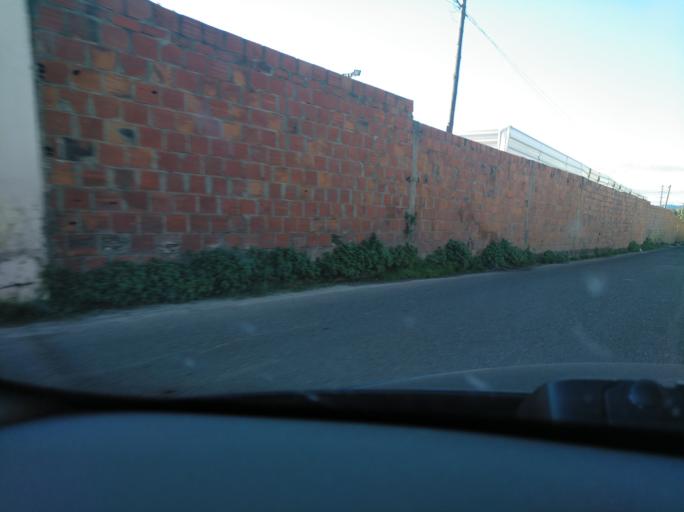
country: PT
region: Lisbon
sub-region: Odivelas
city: Pontinha
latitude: 38.7712
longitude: -9.1807
